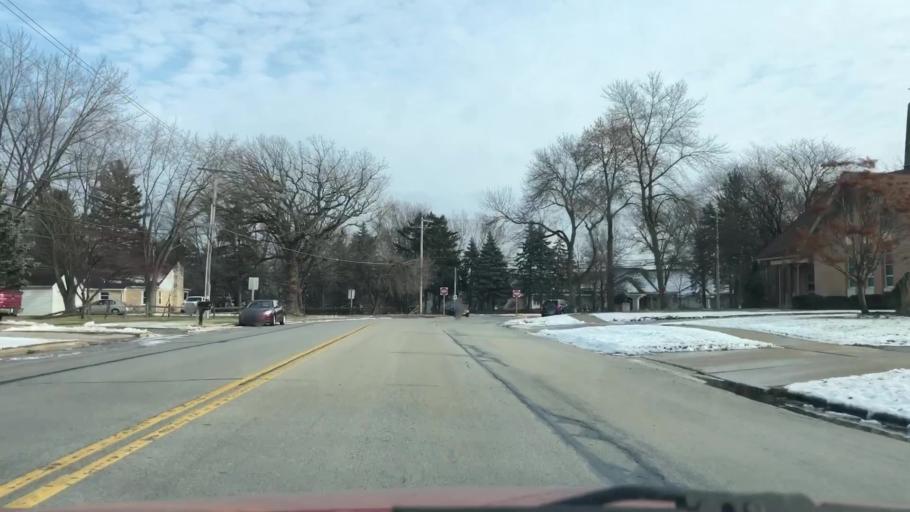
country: US
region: Wisconsin
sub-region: Brown County
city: De Pere
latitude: 44.4305
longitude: -88.0789
